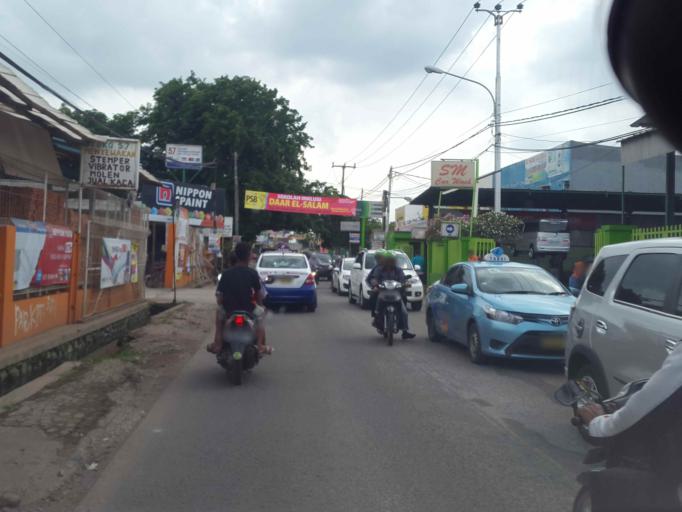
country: ID
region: West Java
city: Bekasi
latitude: -6.3030
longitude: 106.9566
